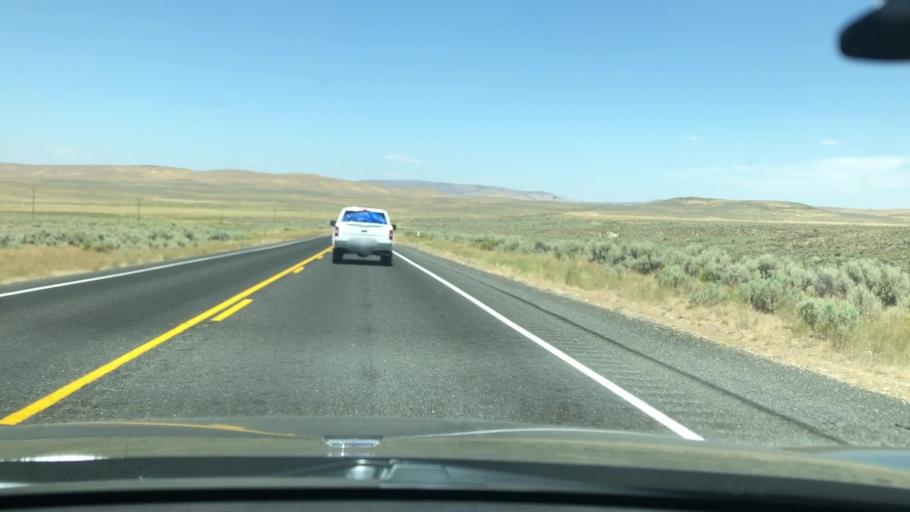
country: US
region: Idaho
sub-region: Owyhee County
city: Murphy
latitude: 43.0334
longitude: -117.0678
